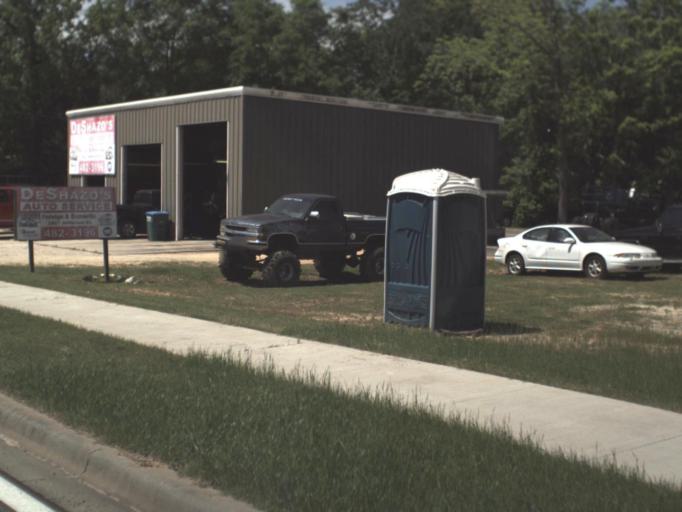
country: US
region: Florida
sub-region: Jackson County
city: Marianna
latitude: 30.7697
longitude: -85.2269
